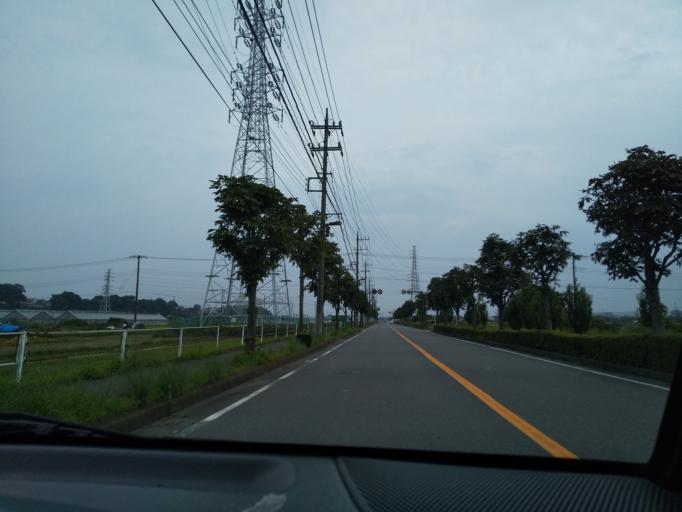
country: JP
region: Kanagawa
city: Atsugi
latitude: 35.4420
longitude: 139.3909
